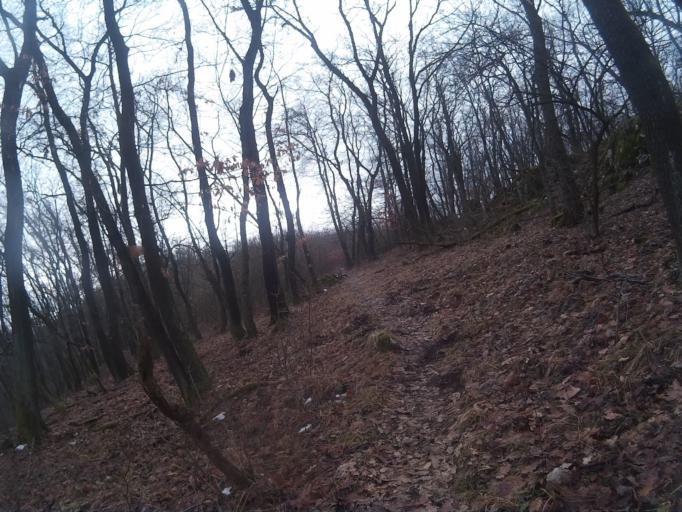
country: HU
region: Komarom-Esztergom
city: Tarjan
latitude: 47.6381
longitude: 18.4799
